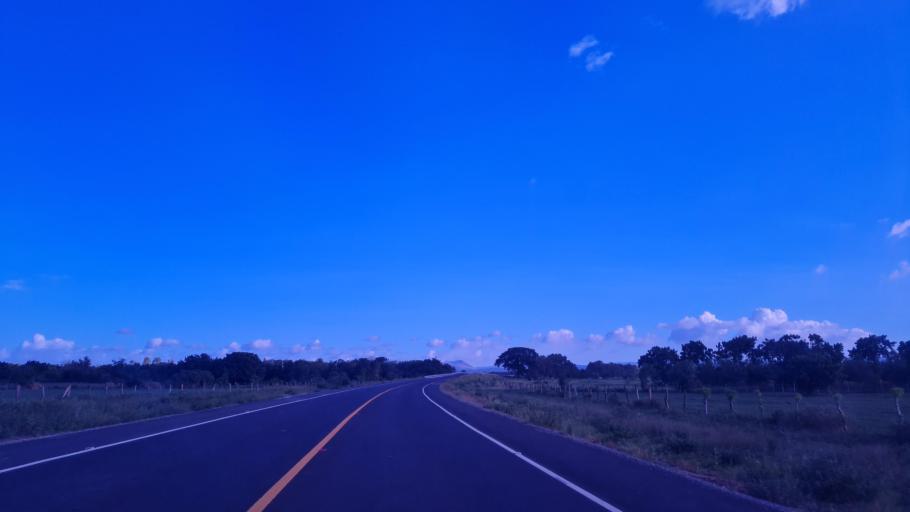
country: NI
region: Managua
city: Tipitapa
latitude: 12.1144
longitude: -86.1521
